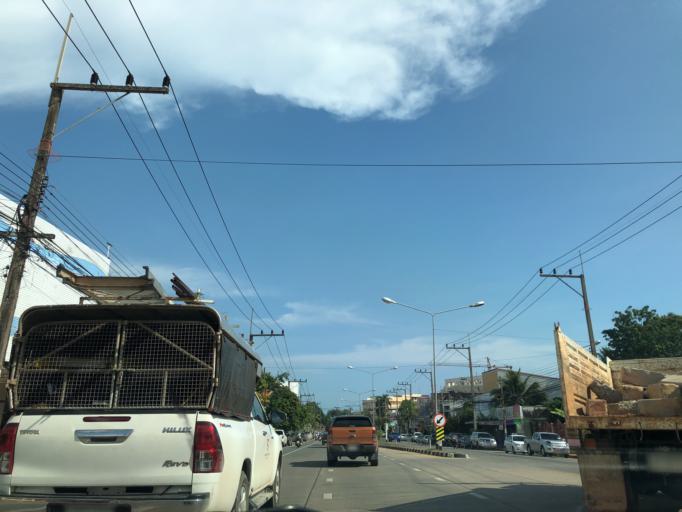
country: TH
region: Krabi
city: Krabi
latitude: 8.0792
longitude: 98.9152
